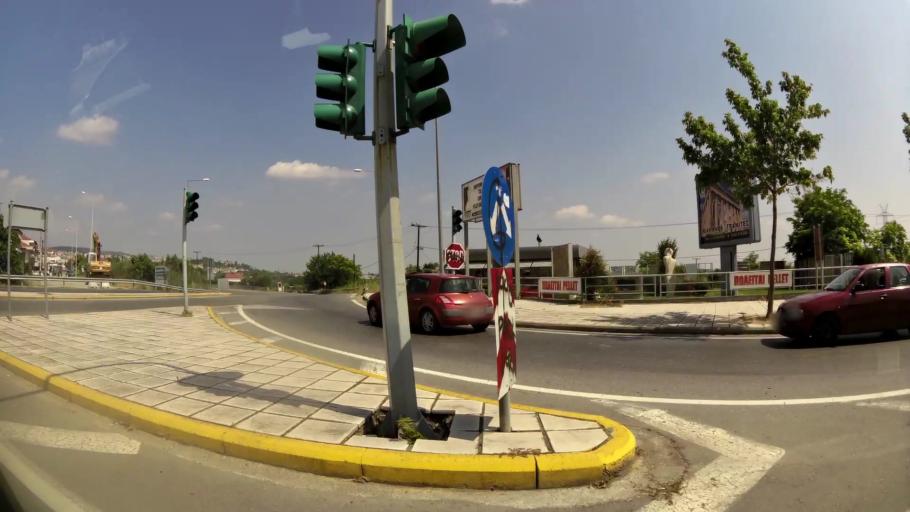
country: GR
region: Central Macedonia
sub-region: Nomos Imathias
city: Veroia
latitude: 40.5096
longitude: 22.2187
